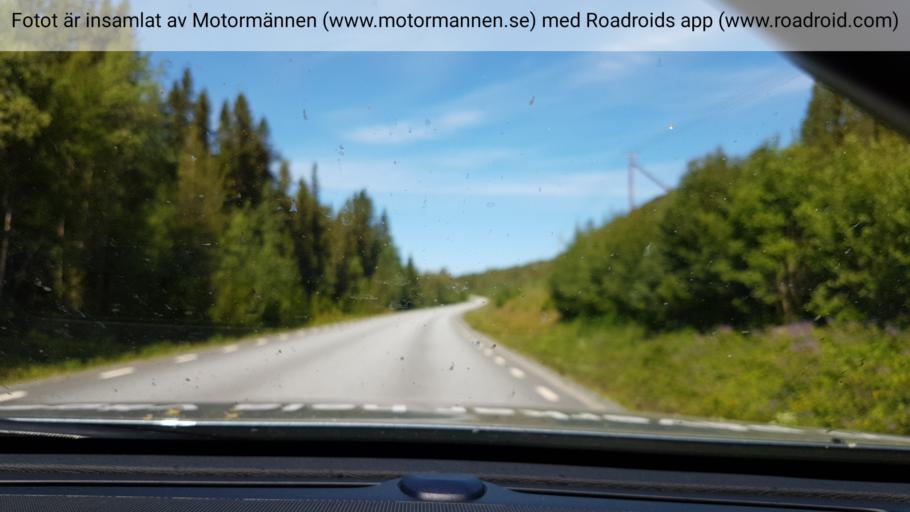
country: SE
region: Vaesterbotten
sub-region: Vilhelmina Kommun
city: Sjoberg
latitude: 64.6659
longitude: 15.6148
